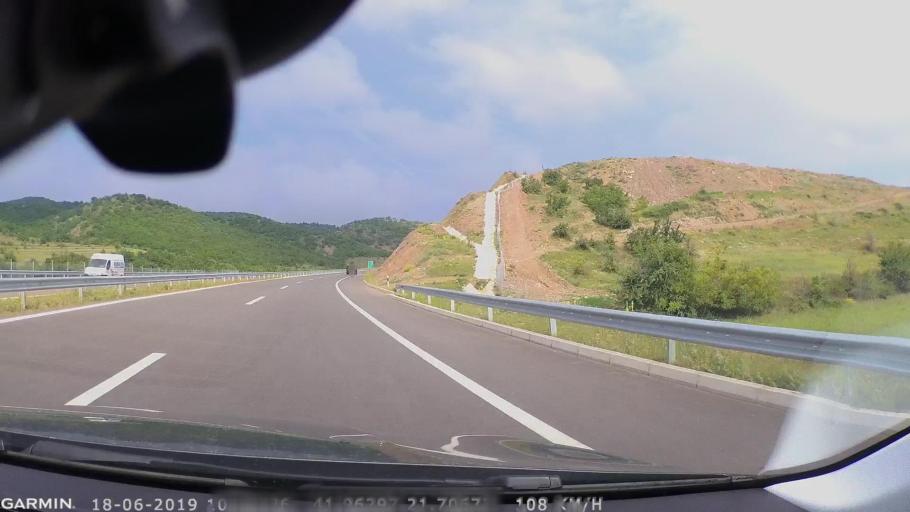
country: MK
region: Petrovec
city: Sredno Konjare
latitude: 41.9475
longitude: 21.7987
